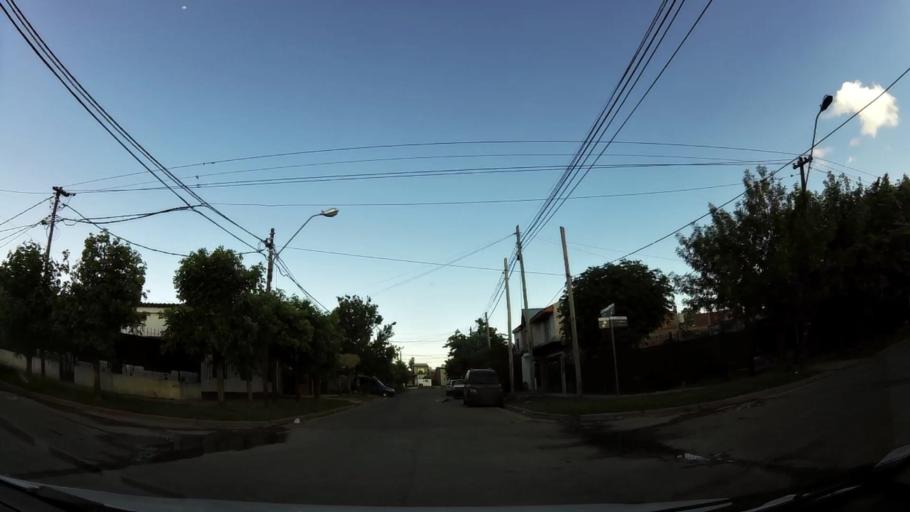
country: AR
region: Buenos Aires
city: Ituzaingo
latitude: -34.6959
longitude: -58.6390
